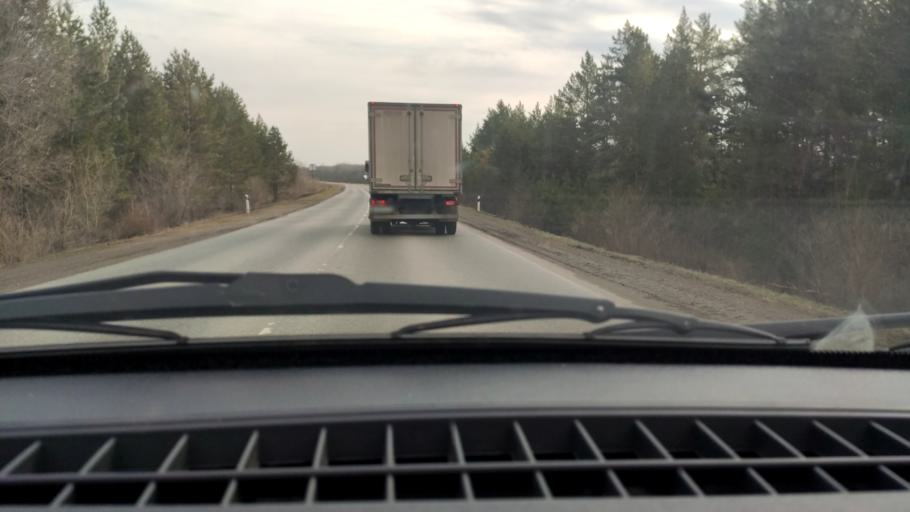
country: RU
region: Bashkortostan
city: Davlekanovo
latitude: 54.2455
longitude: 55.0748
